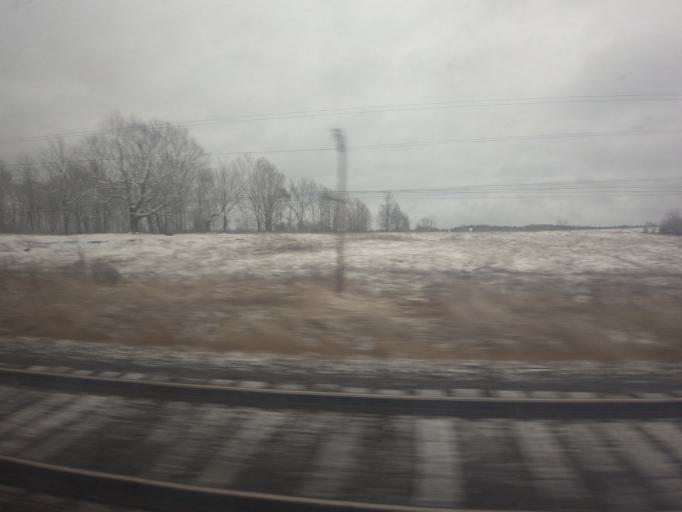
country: US
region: New York
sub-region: Jefferson County
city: Alexandria Bay
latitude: 44.3934
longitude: -76.0380
